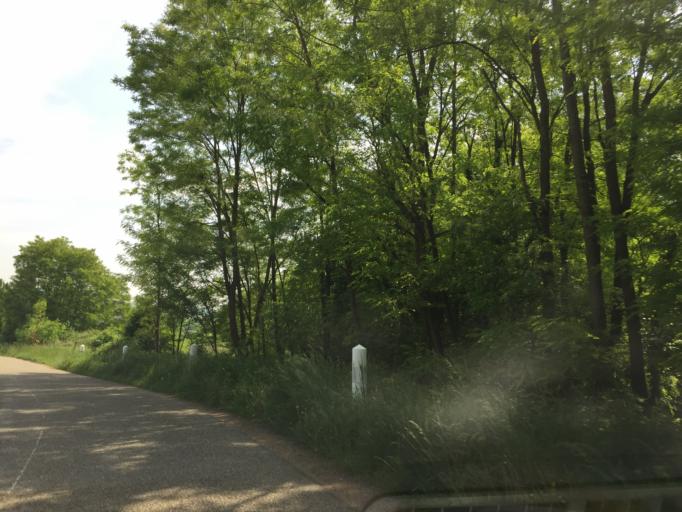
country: FR
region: Alsace
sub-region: Departement du Bas-Rhin
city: Durrenbach
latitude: 48.9096
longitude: 7.7408
